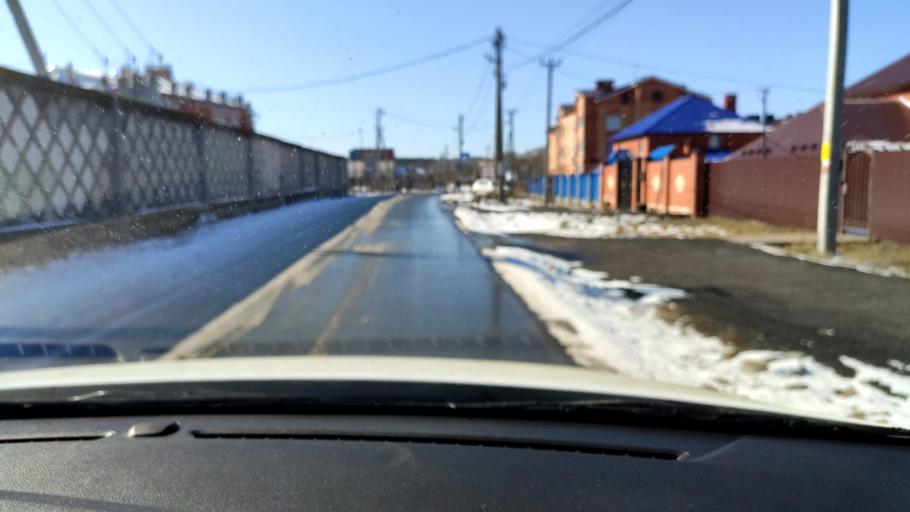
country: RU
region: Tatarstan
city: Vysokaya Gora
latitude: 55.8746
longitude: 49.2455
